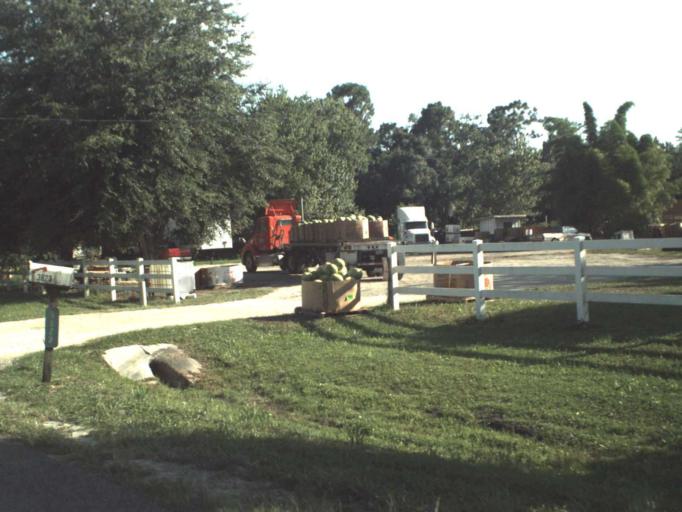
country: US
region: Florida
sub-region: Lake County
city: Groveland
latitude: 28.4034
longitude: -81.8287
